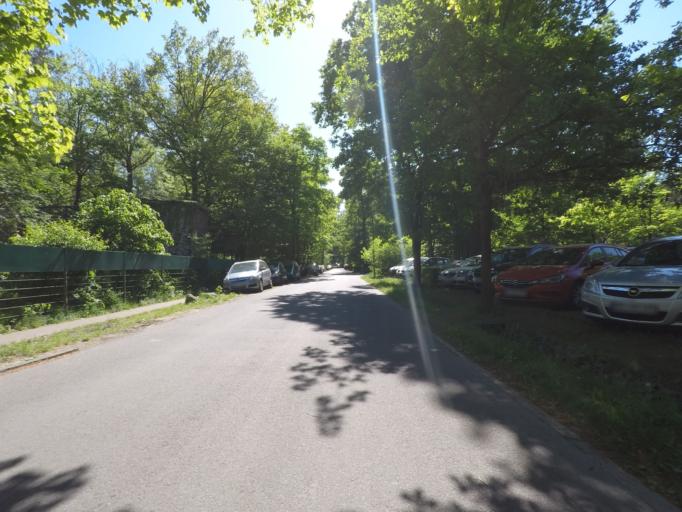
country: DE
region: Brandenburg
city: Eberswalde
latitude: 52.8241
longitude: 13.7811
